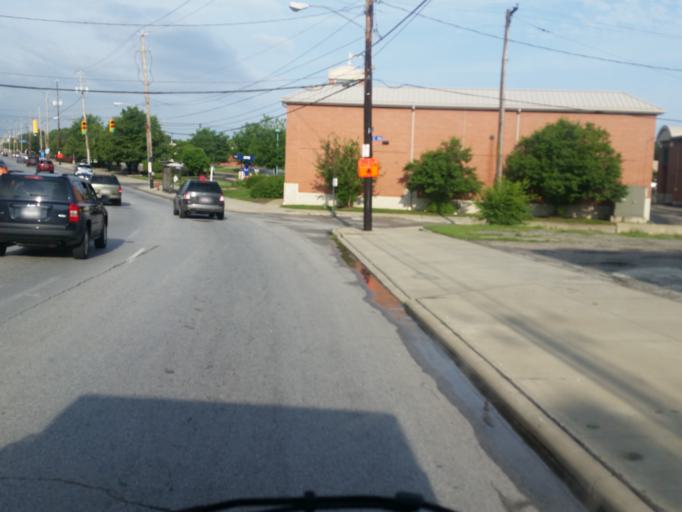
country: US
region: Ohio
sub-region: Cuyahoga County
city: Bratenahl
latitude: 41.5401
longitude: -81.6126
